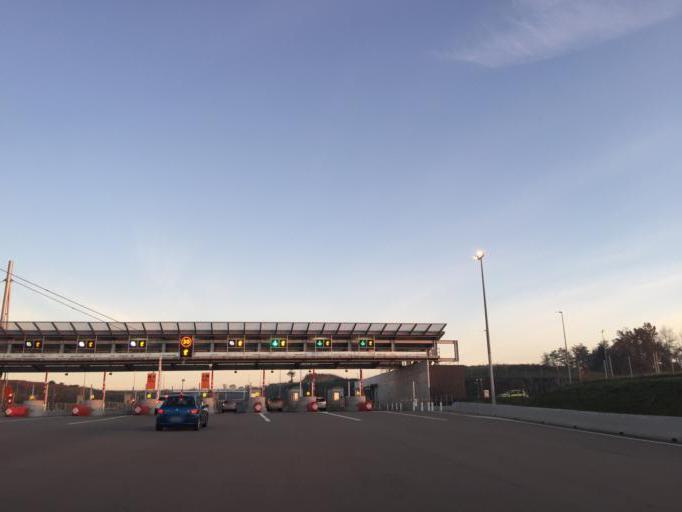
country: FR
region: Rhone-Alpes
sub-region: Departement de la Loire
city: Balbigny
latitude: 45.8403
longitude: 4.1645
